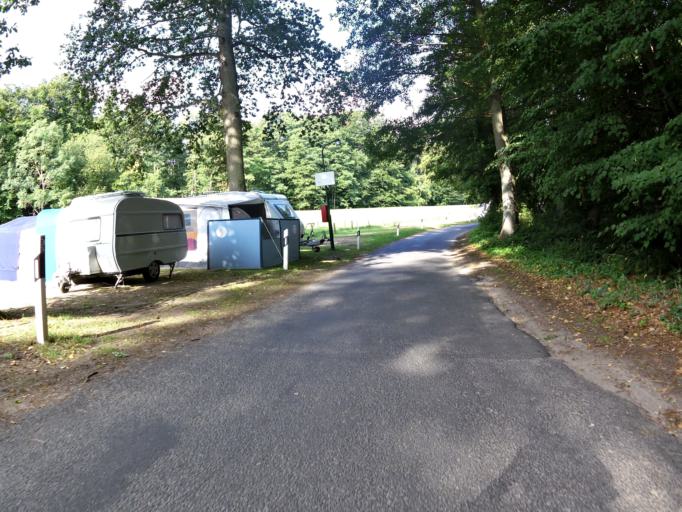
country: DE
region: Mecklenburg-Vorpommern
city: Seebad Bansin
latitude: 53.9959
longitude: 14.1052
